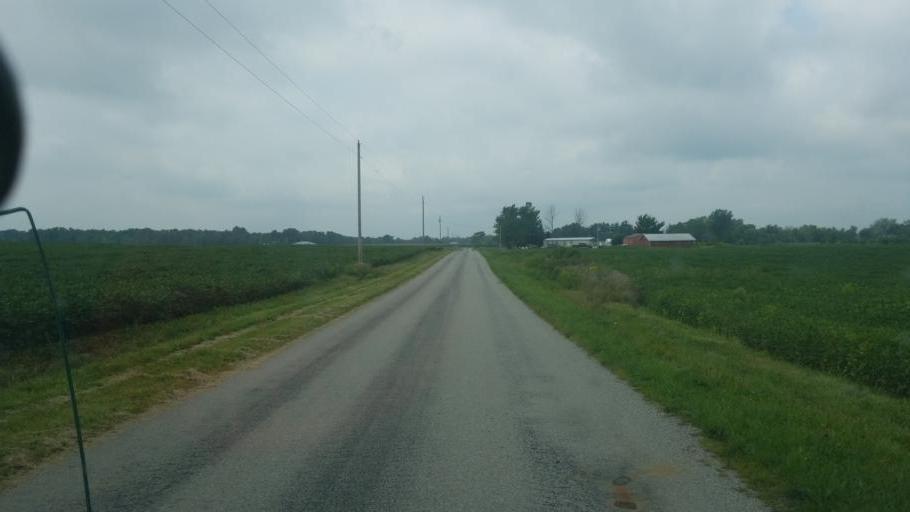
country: US
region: Ohio
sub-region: Huron County
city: Greenwich
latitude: 41.0107
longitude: -82.5029
